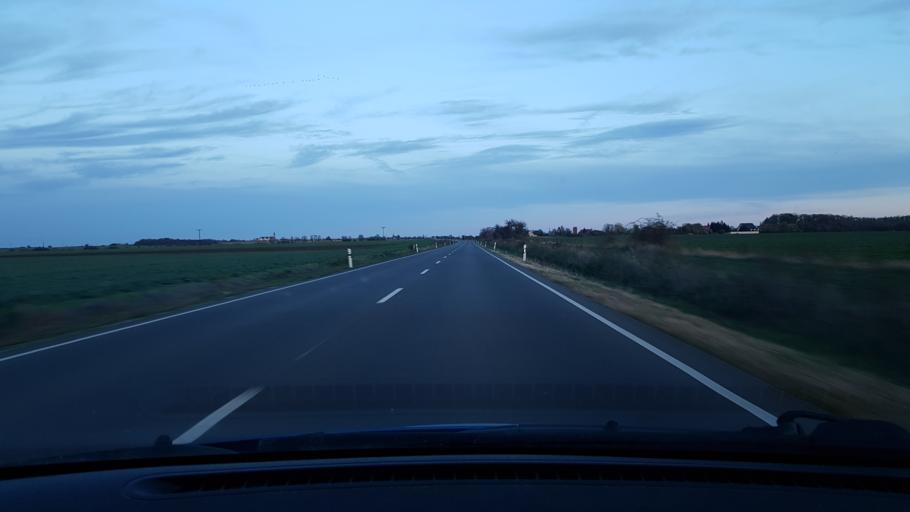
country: DE
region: Saxony-Anhalt
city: Leitzkau
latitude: 52.0649
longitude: 11.8974
